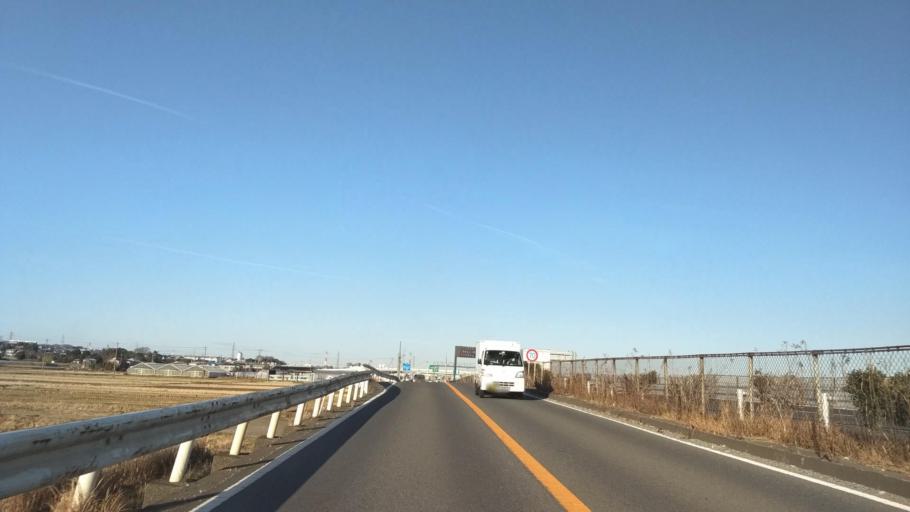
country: JP
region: Kanagawa
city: Isehara
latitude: 35.3816
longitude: 139.3294
